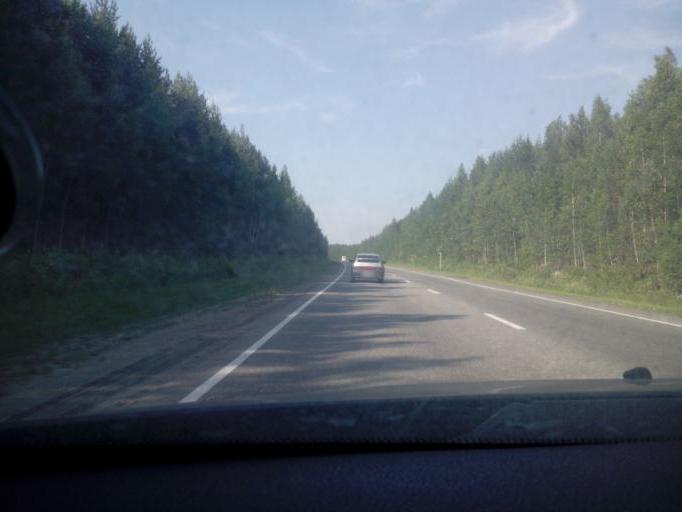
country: RU
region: Sverdlovsk
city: Verkh-Neyvinskiy
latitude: 57.2594
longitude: 60.2884
